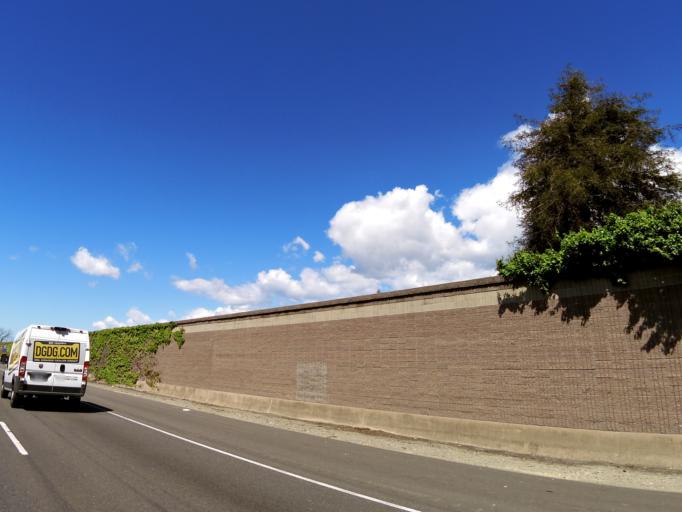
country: US
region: California
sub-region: Alameda County
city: San Leandro
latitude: 37.6985
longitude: -122.1490
